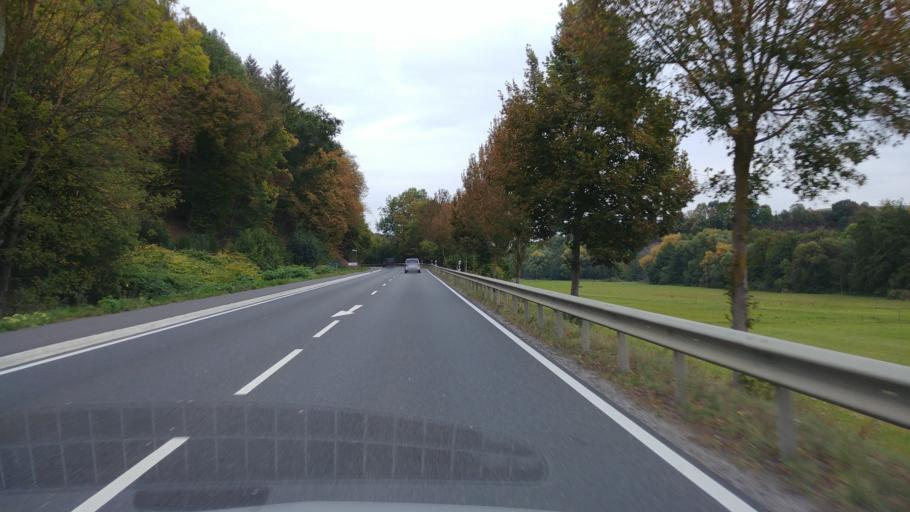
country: DE
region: Rheinland-Pfalz
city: Holzheim
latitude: 50.3554
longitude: 8.0360
